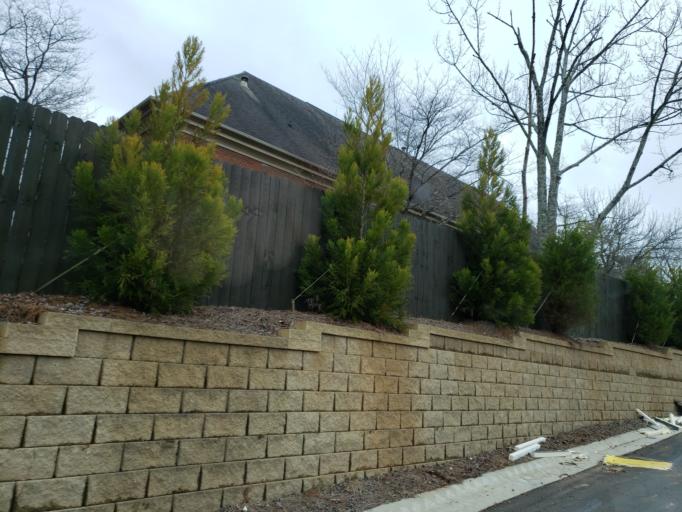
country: US
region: Georgia
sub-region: DeKalb County
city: Dunwoody
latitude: 33.9480
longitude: -84.3312
